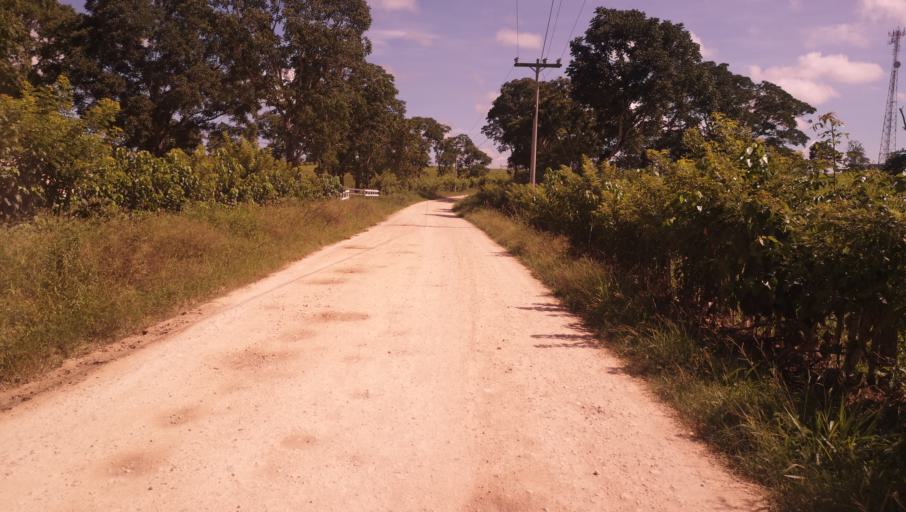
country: GT
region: Peten
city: Melchor de Mencos
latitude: 16.8415
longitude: -89.2987
